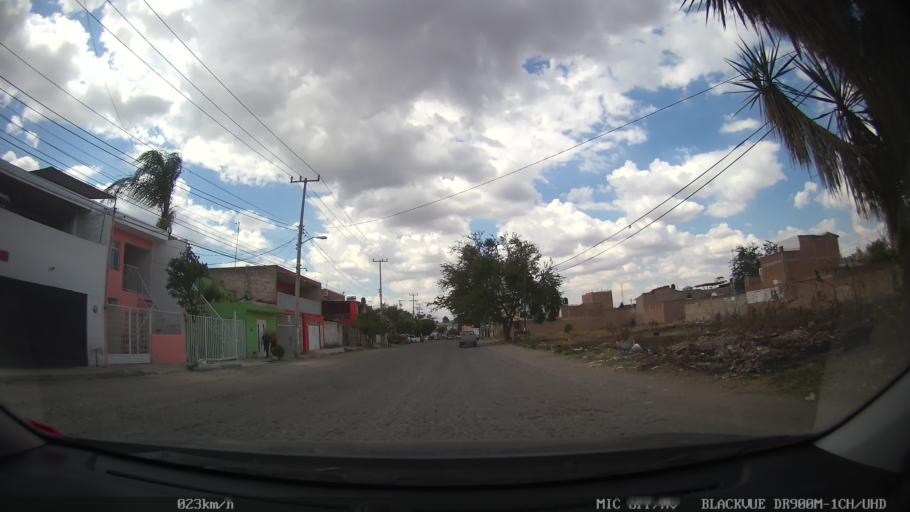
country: MX
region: Jalisco
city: Tlaquepaque
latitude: 20.6722
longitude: -103.2603
